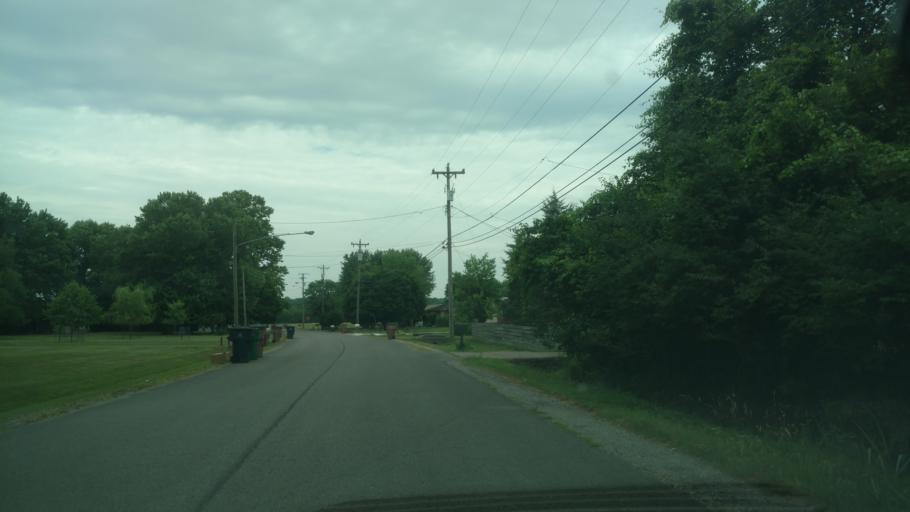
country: US
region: Tennessee
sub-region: Davidson County
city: Nashville
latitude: 36.1896
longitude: -86.7072
